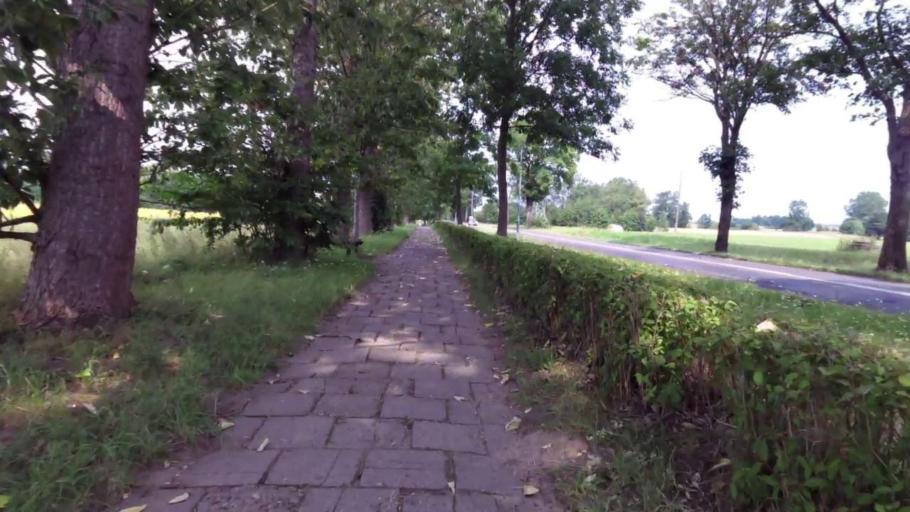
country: PL
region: West Pomeranian Voivodeship
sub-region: Powiat drawski
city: Drawsko Pomorskie
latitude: 53.5477
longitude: 15.8204
